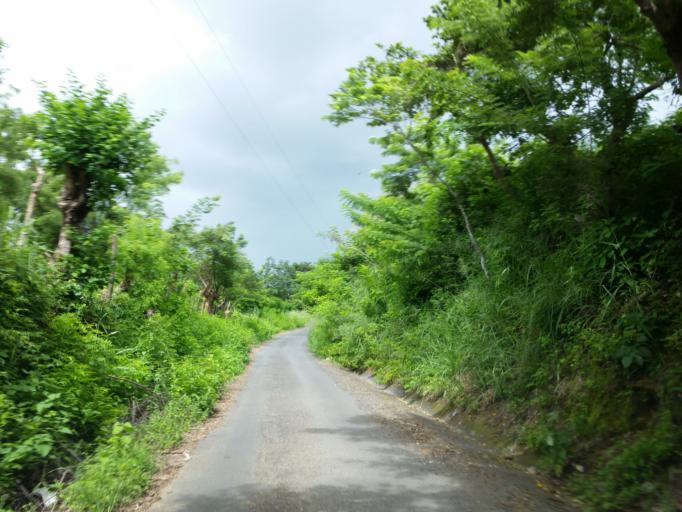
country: NI
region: Masaya
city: Ticuantepe
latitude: 12.0592
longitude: -86.2400
